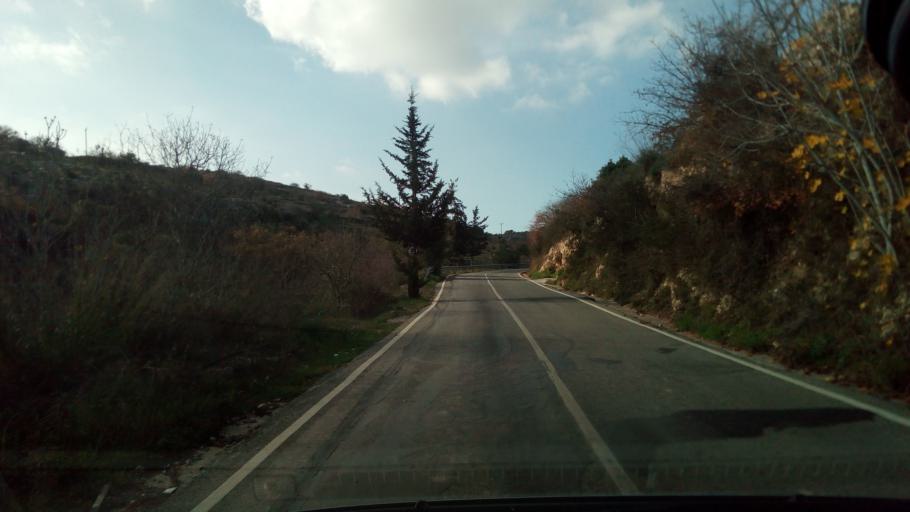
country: CY
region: Pafos
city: Pegeia
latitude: 34.9547
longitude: 32.4187
